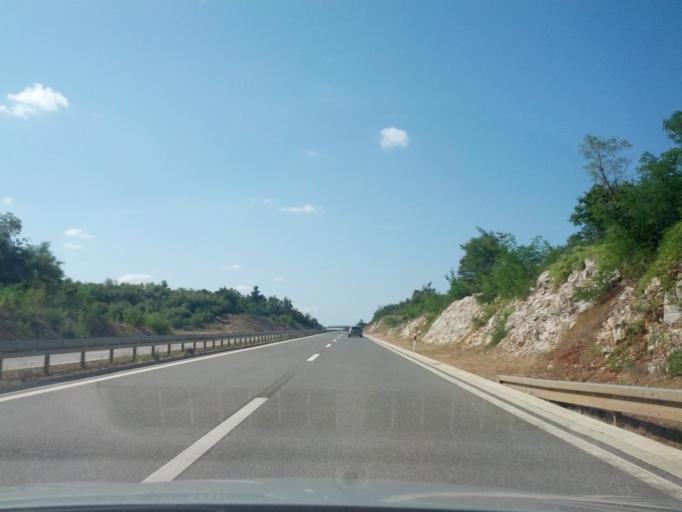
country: HR
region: Istarska
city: Vrsar
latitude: 45.1973
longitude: 13.7301
